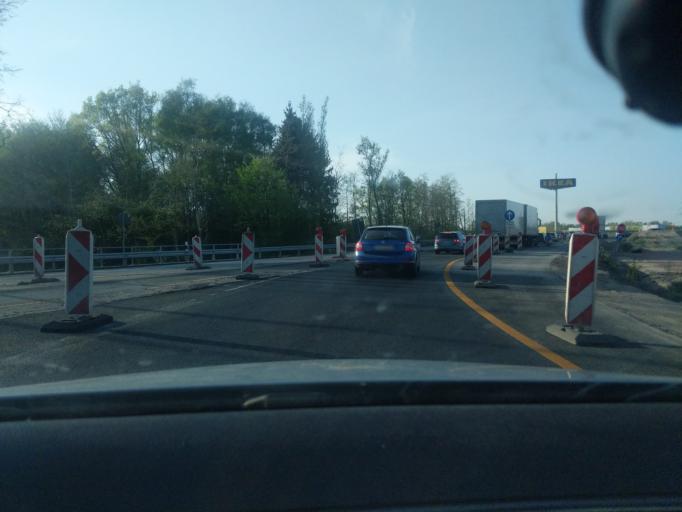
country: DE
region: Schleswig-Holstein
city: Bonningstedt
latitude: 53.6454
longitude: 9.9291
